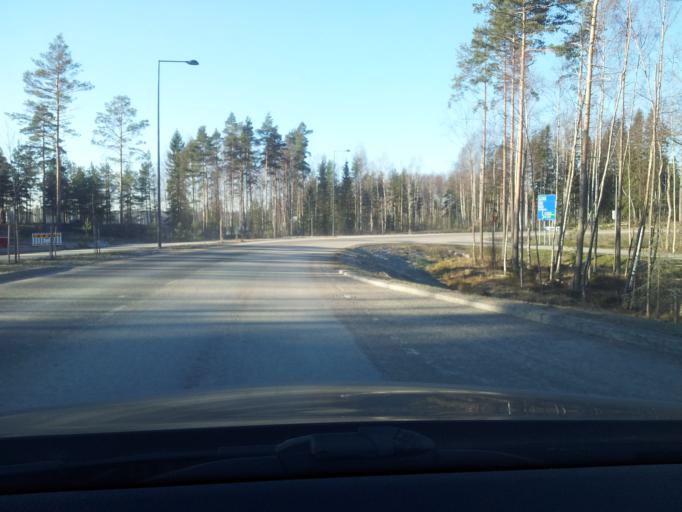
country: FI
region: Uusimaa
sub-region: Helsinki
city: Espoo
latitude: 60.1463
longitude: 24.5789
